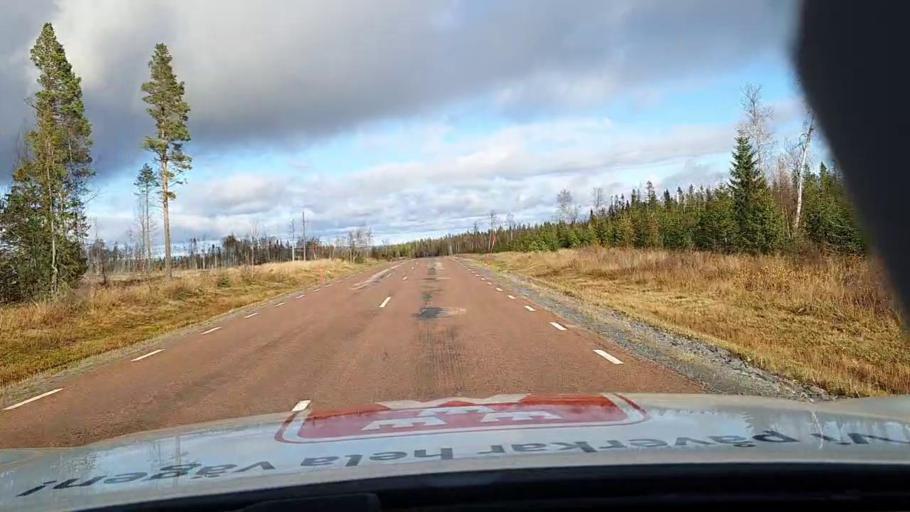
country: SE
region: Jaemtland
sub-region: Krokoms Kommun
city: Valla
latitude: 63.1340
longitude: 13.9387
